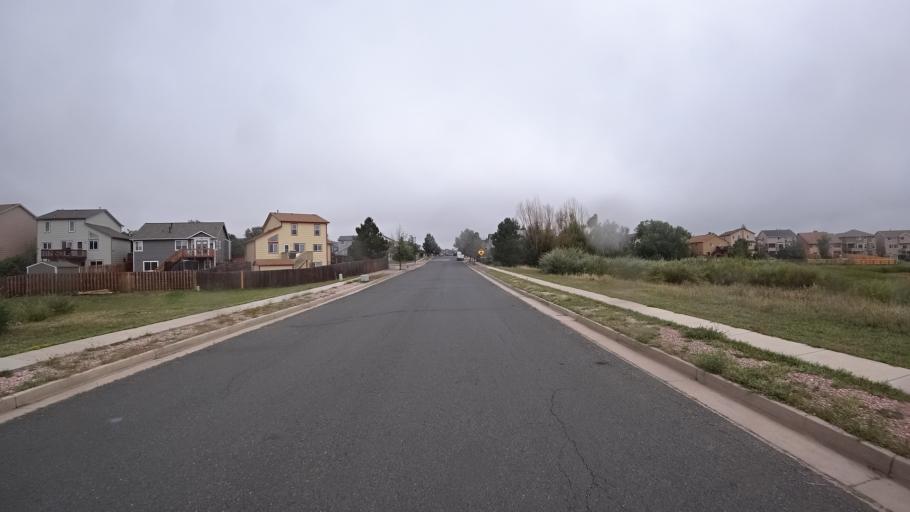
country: US
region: Colorado
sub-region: El Paso County
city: Cimarron Hills
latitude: 38.9260
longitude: -104.7274
